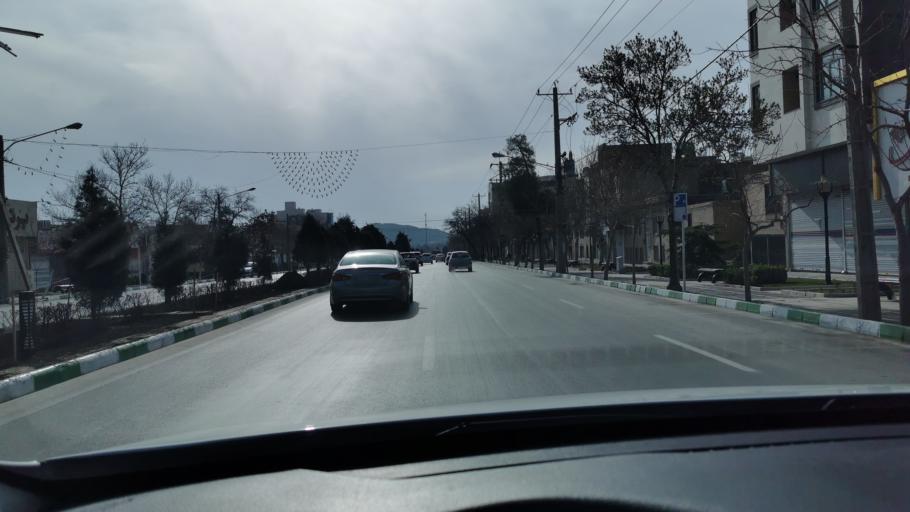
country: IR
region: Razavi Khorasan
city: Mashhad
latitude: 36.2863
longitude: 59.5455
